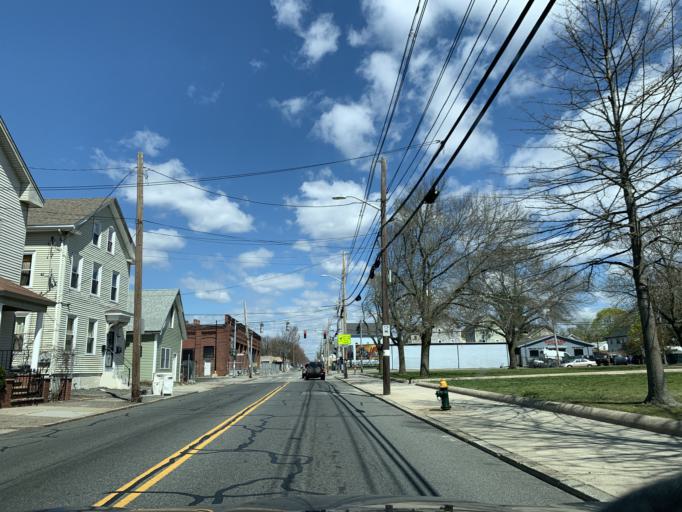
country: US
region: Rhode Island
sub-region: Providence County
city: Providence
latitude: 41.7981
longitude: -71.4116
